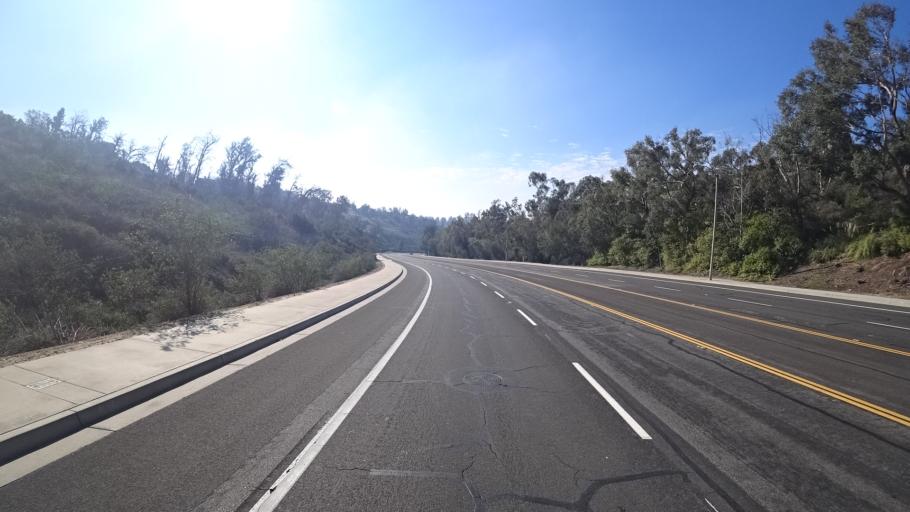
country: US
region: California
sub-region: Orange County
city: North Tustin
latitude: 33.7802
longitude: -117.7767
